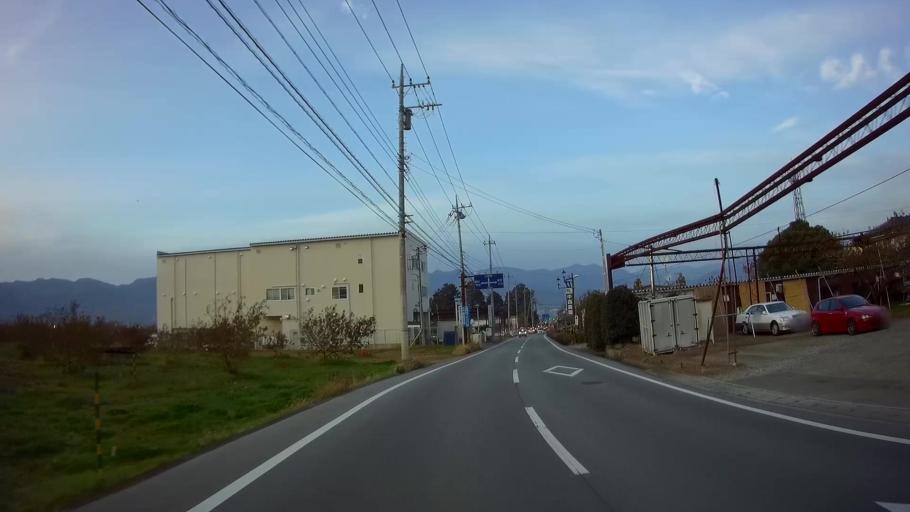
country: JP
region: Yamanashi
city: Isawa
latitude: 35.6420
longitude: 138.6866
